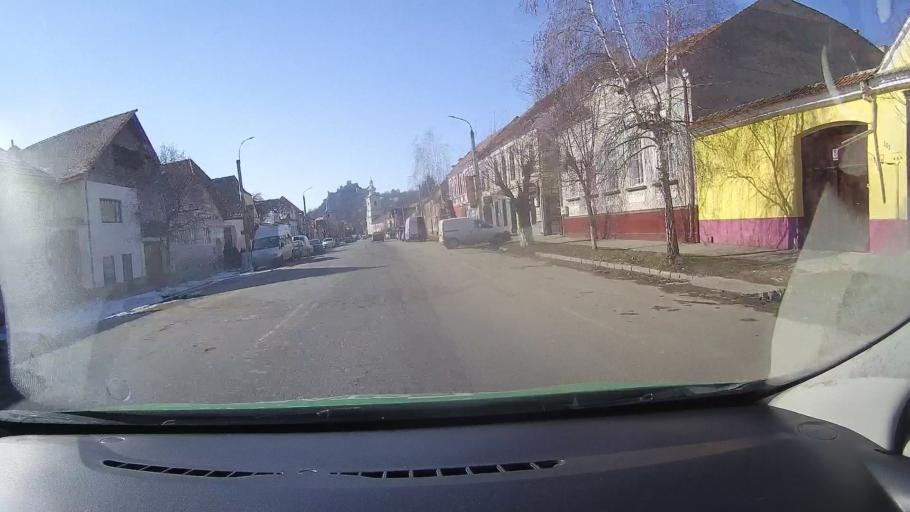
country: RO
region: Brasov
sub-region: Oras Rupea
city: Rupea
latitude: 46.0395
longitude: 25.2259
